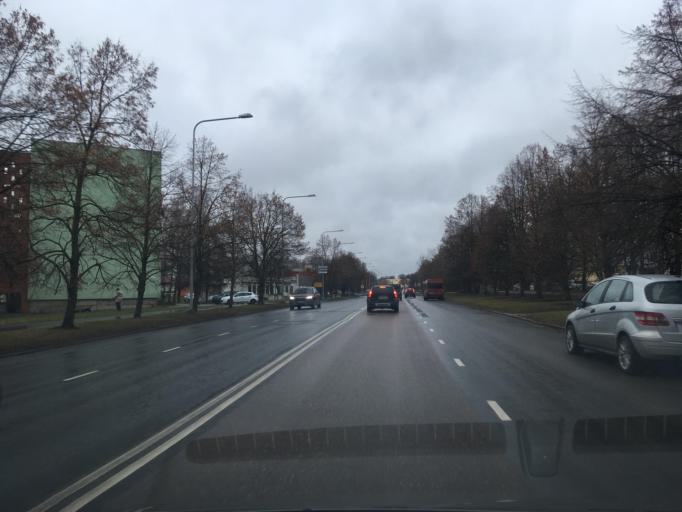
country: EE
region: Tartu
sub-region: Tartu linn
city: Tartu
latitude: 58.3723
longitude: 26.7669
